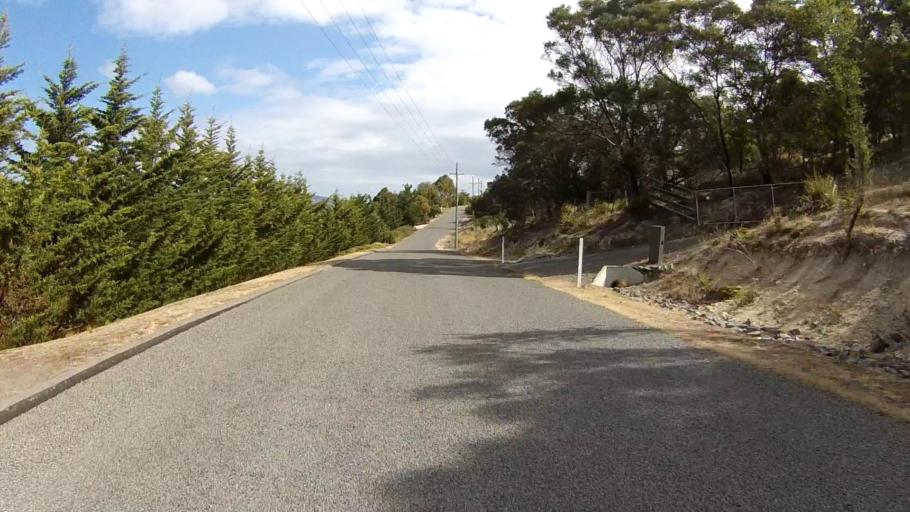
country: AU
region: Tasmania
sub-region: Clarence
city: Acton Park
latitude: -42.8818
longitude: 147.5040
